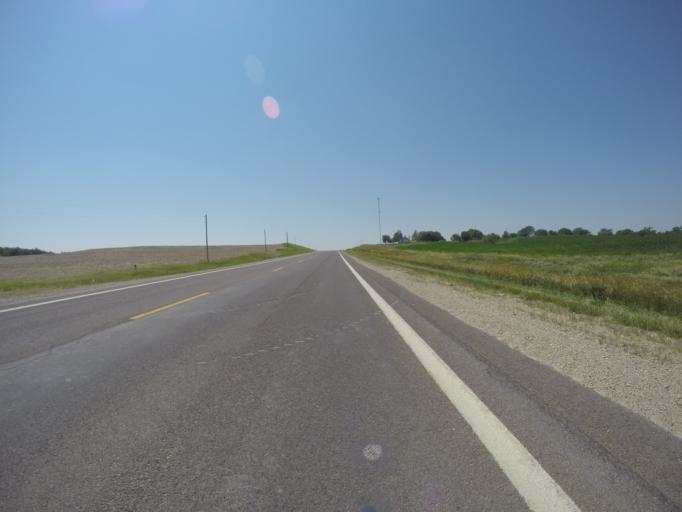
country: US
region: Kansas
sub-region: Doniphan County
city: Highland
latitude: 39.8521
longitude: -95.2652
